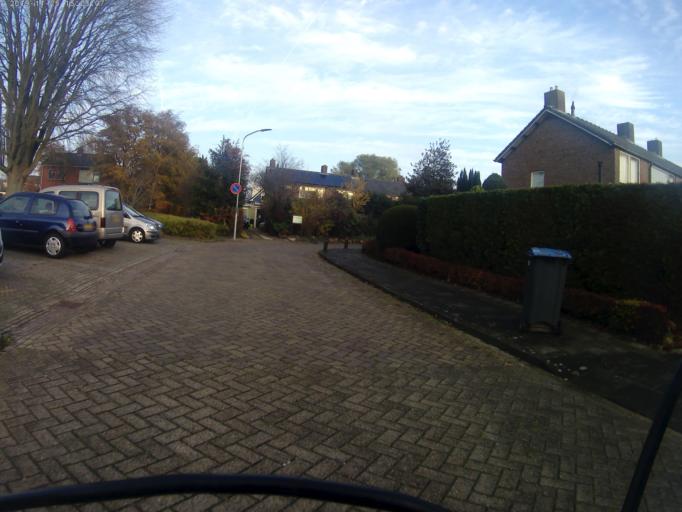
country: NL
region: Drenthe
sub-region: Gemeente Assen
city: Assen
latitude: 52.9995
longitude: 6.5542
